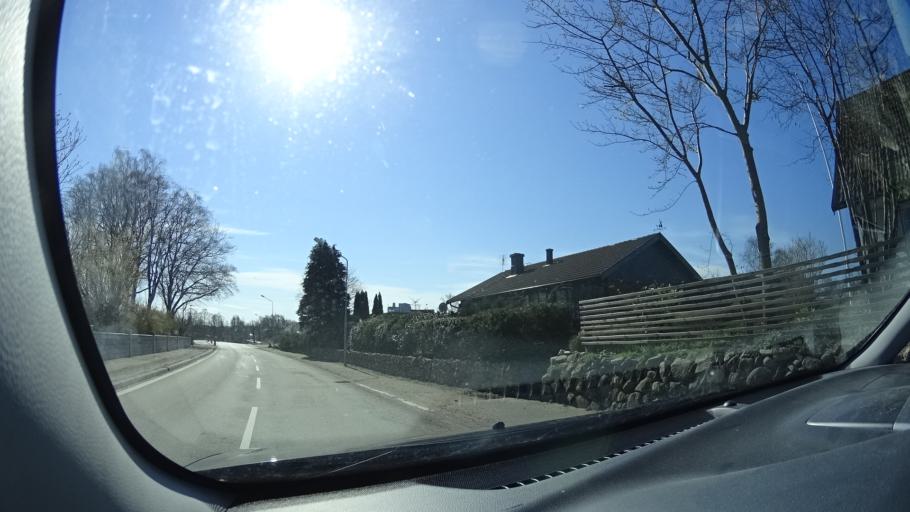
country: SE
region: Skane
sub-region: Hoganas Kommun
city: Hoganas
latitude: 56.2206
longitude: 12.6764
